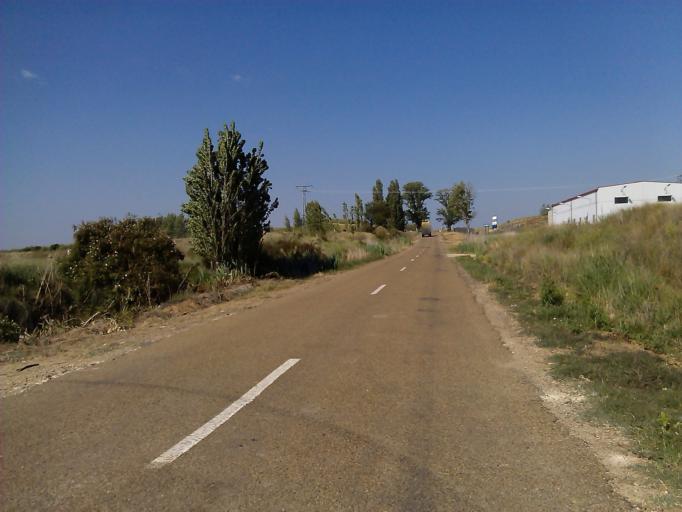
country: ES
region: Castille and Leon
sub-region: Provincia de Palencia
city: Melgar de Yuso
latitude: 42.2670
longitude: -4.2712
